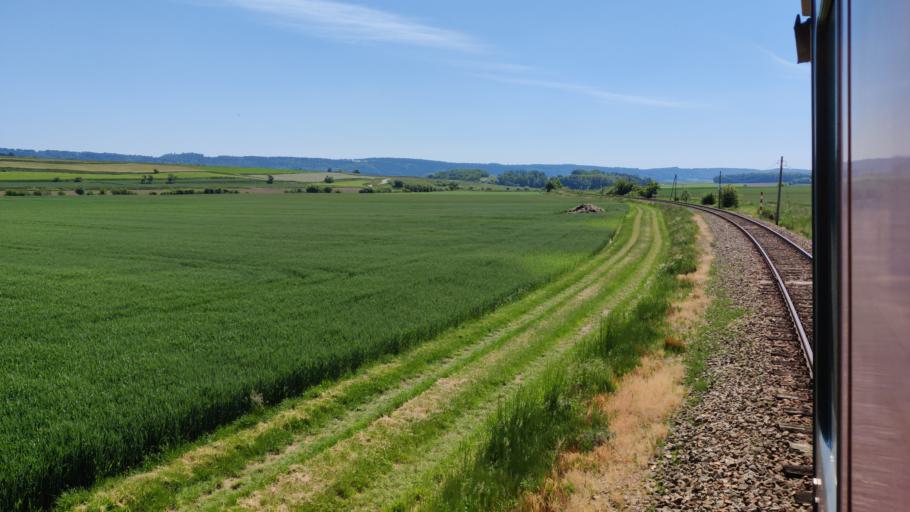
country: AT
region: Lower Austria
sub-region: Politischer Bezirk Horn
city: Horn
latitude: 48.6474
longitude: 15.6794
